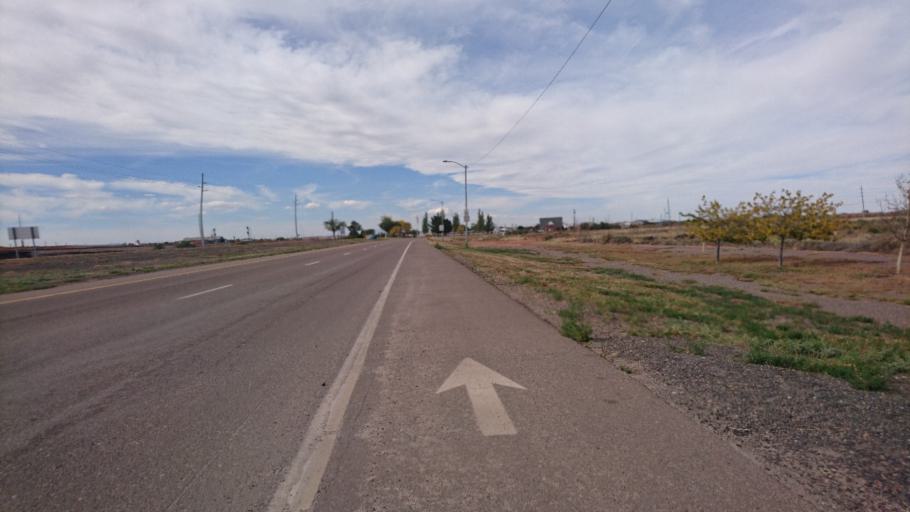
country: US
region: Arizona
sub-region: Navajo County
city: Winslow
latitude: 35.0143
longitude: -110.6769
